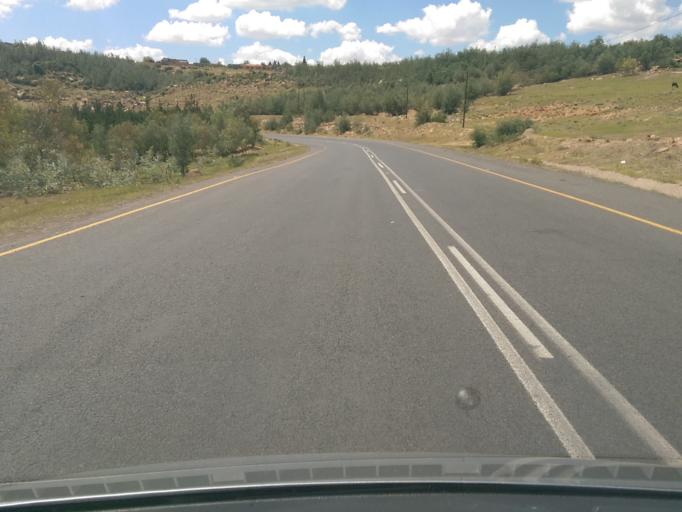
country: LS
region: Maseru
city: Maseru
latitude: -29.3970
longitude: 27.5293
